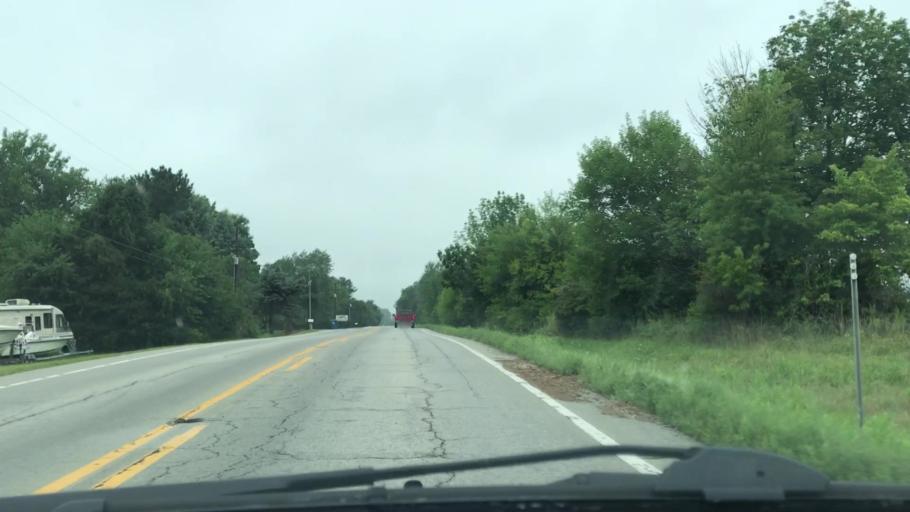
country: US
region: Indiana
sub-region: Hamilton County
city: Westfield
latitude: 40.0832
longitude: -86.1018
